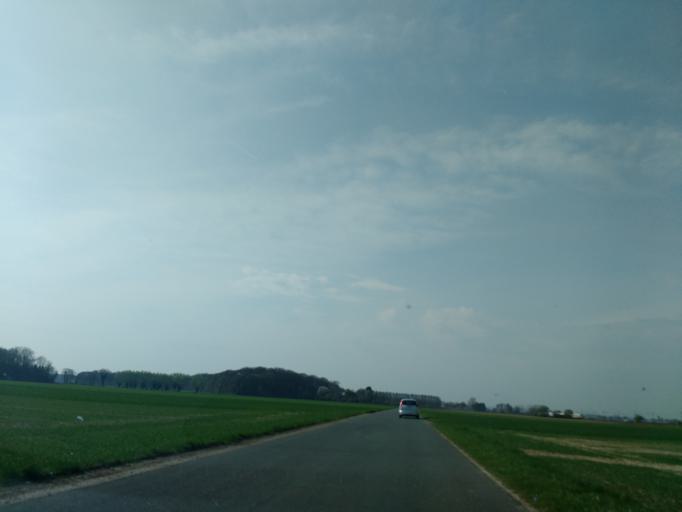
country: DE
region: North Rhine-Westphalia
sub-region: Regierungsbezirk Detmold
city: Salzkotten
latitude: 51.7078
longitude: 8.6443
